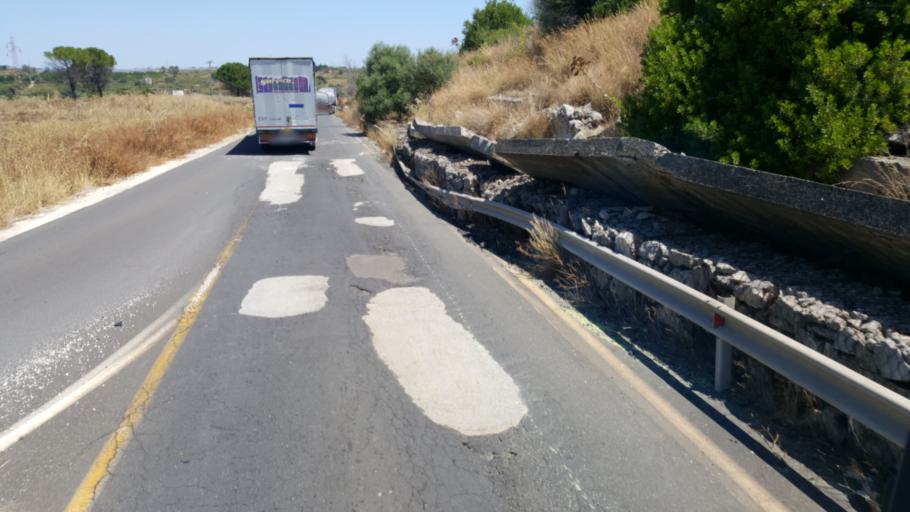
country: IT
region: Sicily
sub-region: Provincia di Siracusa
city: Melilli
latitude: 37.2159
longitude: 15.1546
